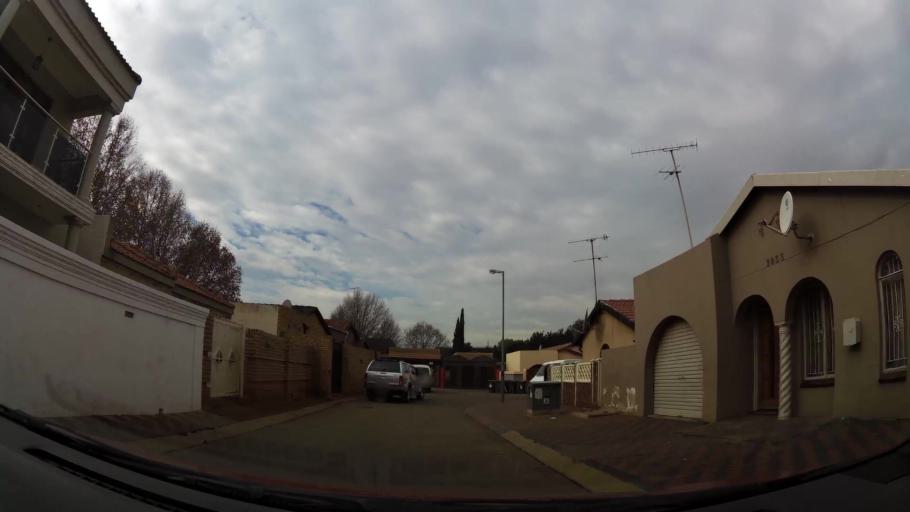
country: ZA
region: Gauteng
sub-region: City of Johannesburg Metropolitan Municipality
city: Soweto
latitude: -26.2725
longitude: 27.8305
